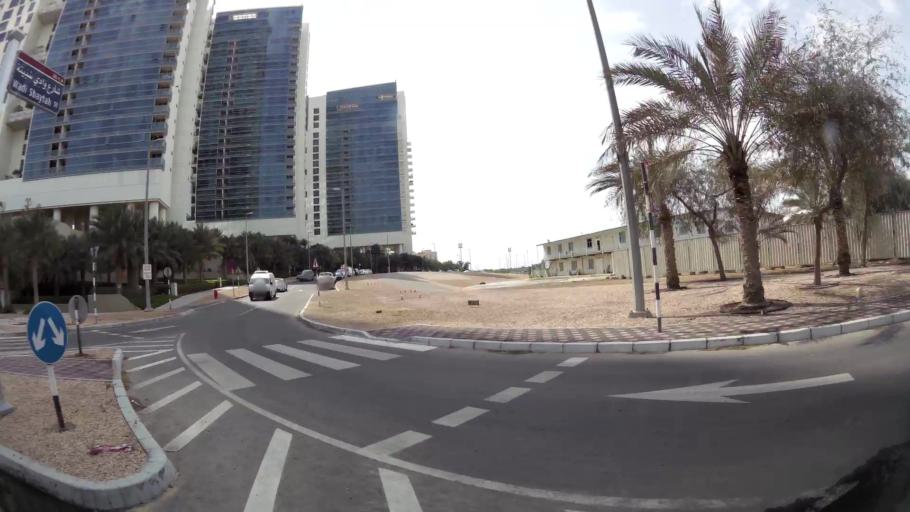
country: AE
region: Abu Dhabi
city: Abu Dhabi
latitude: 24.4152
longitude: 54.4626
